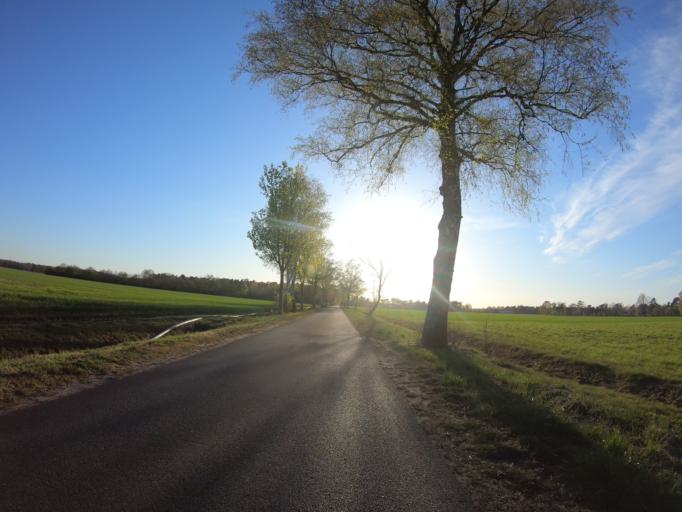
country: DE
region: Lower Saxony
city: Sassenburg
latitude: 52.4799
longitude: 10.6099
